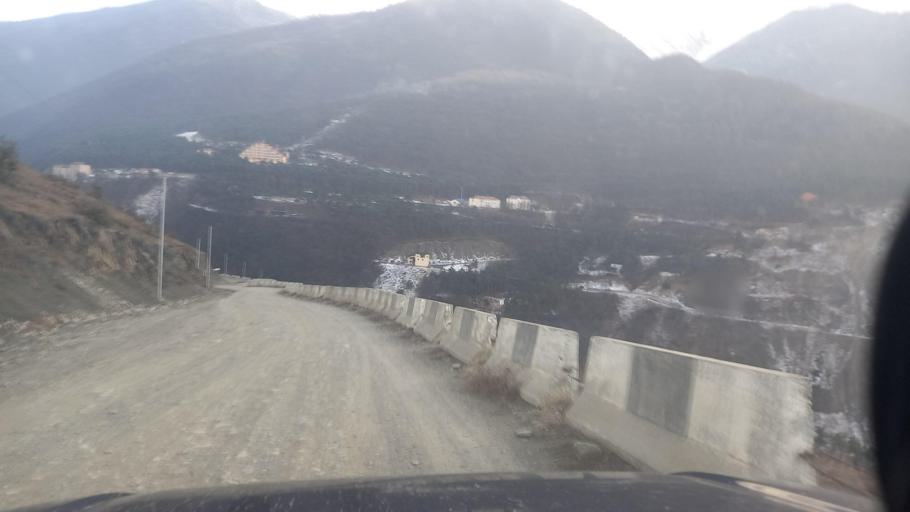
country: RU
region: Ingushetiya
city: Dzhayrakh
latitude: 42.8192
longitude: 44.7028
